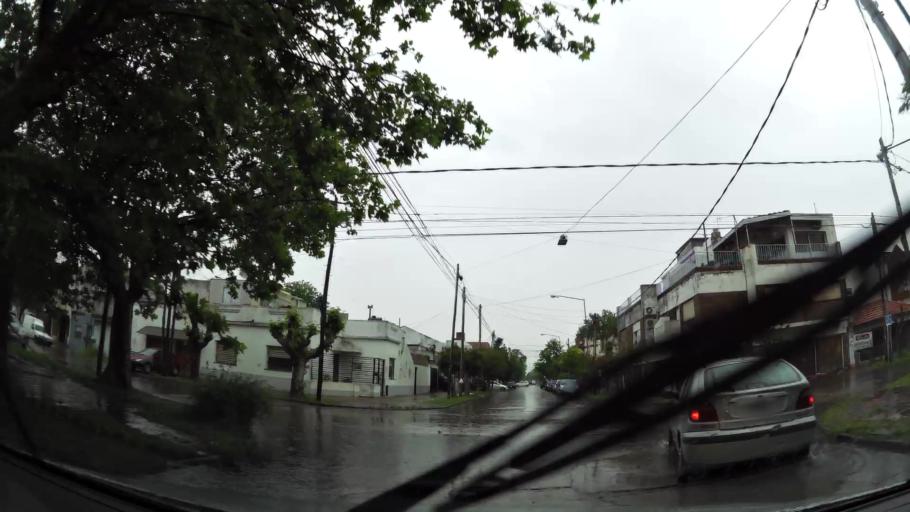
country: AR
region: Buenos Aires
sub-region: Partido de Lanus
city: Lanus
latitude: -34.7193
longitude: -58.3963
